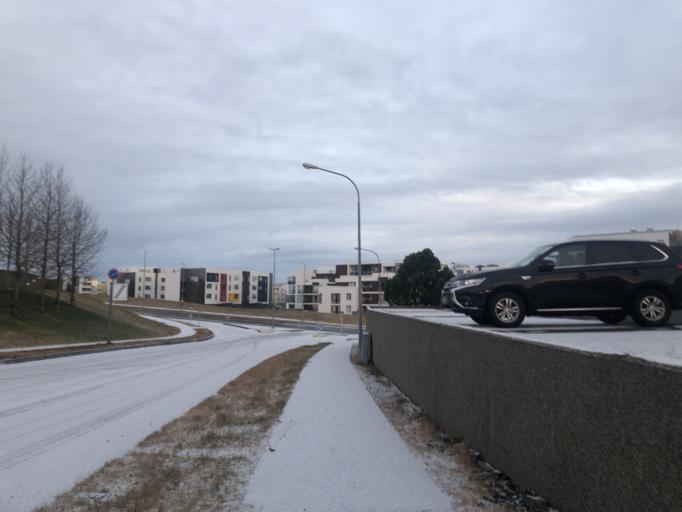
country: IS
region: Capital Region
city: Gardabaer
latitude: 64.0912
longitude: -21.9371
